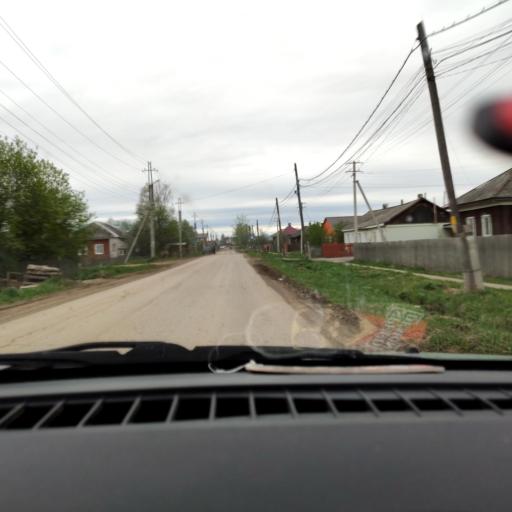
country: RU
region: Perm
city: Kudymkar
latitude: 59.0099
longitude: 54.6418
